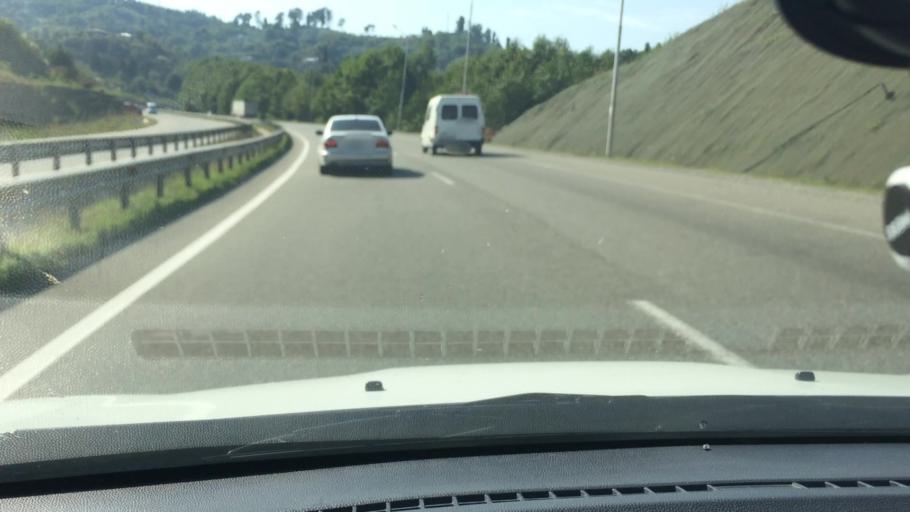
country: GE
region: Ajaria
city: Makhinjauri
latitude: 41.6991
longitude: 41.7286
